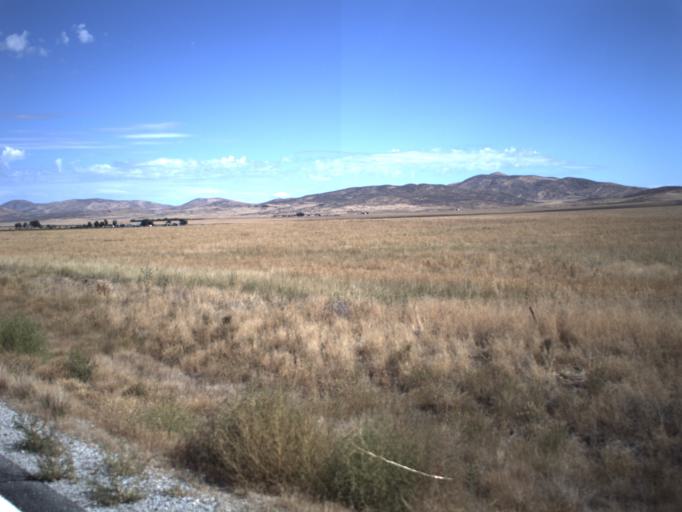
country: US
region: Utah
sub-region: Box Elder County
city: Tremonton
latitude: 41.7240
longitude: -112.4337
